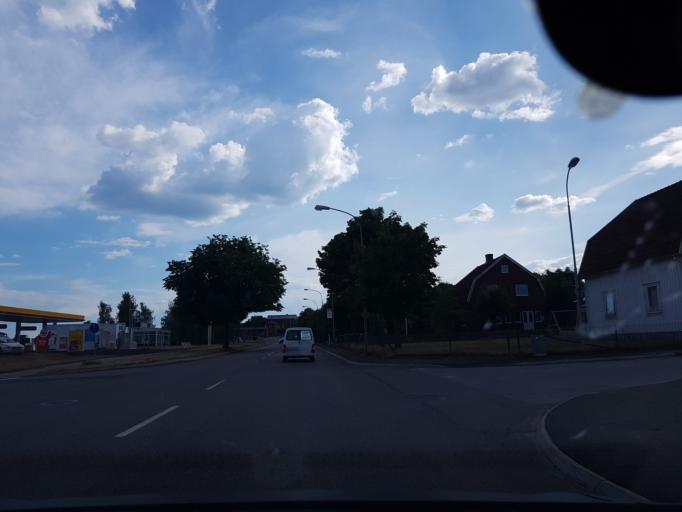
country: SE
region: Joenkoeping
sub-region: Gislaveds Kommun
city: Gislaved
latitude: 57.3077
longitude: 13.5421
